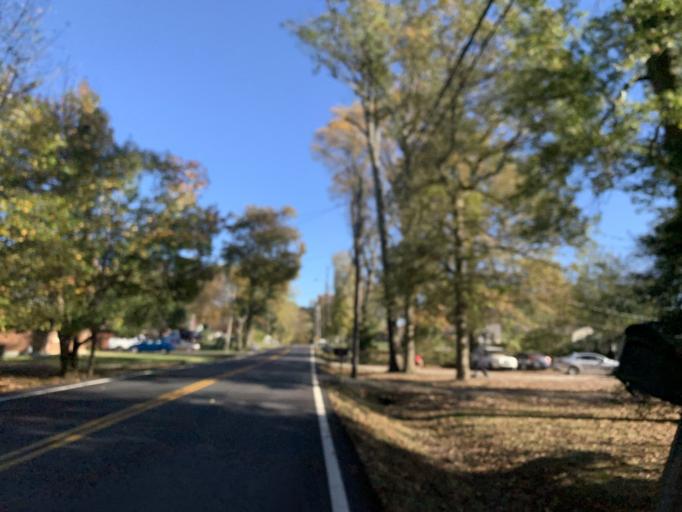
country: US
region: Kentucky
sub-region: Jefferson County
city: Pleasure Ridge Park
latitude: 38.1568
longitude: -85.8732
